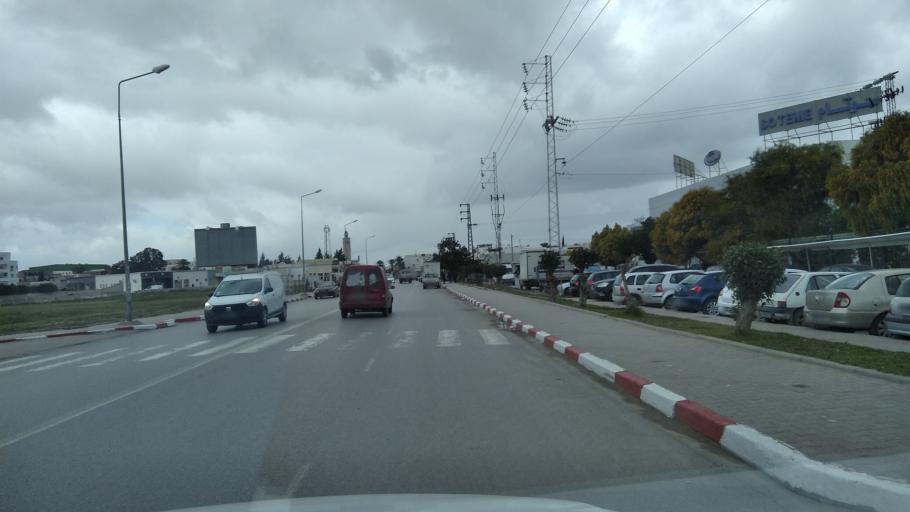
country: TN
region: Bin 'Arus
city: Ben Arous
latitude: 36.7492
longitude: 10.2281
